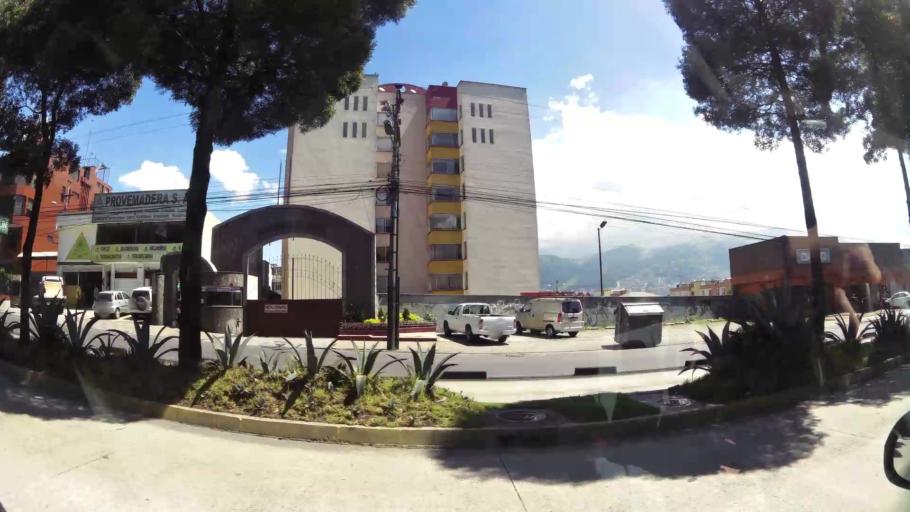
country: EC
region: Pichincha
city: Quito
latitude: -0.2648
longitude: -78.5254
